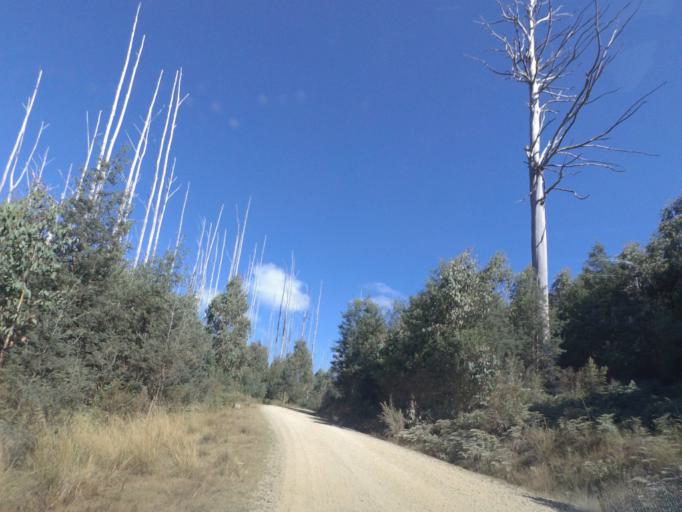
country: AU
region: Victoria
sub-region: Murrindindi
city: Alexandra
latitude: -37.4096
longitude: 145.8068
